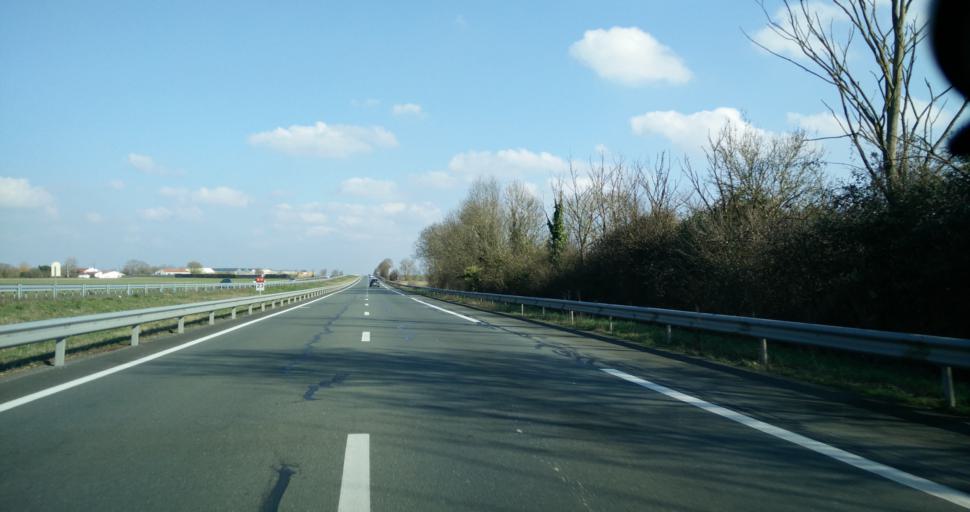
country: FR
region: Poitou-Charentes
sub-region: Departement de la Charente-Maritime
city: Verines
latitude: 46.2163
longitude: -0.9824
